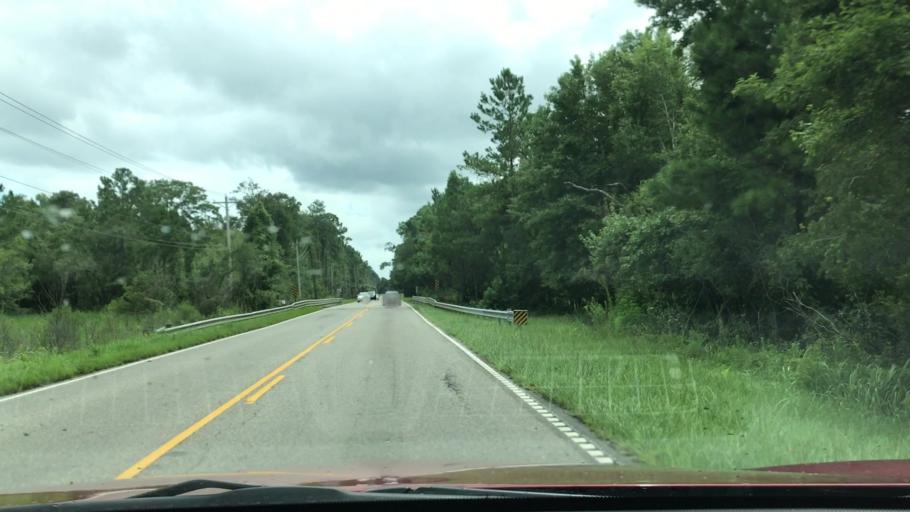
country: US
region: South Carolina
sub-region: Georgetown County
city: Georgetown
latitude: 33.4700
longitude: -79.2795
